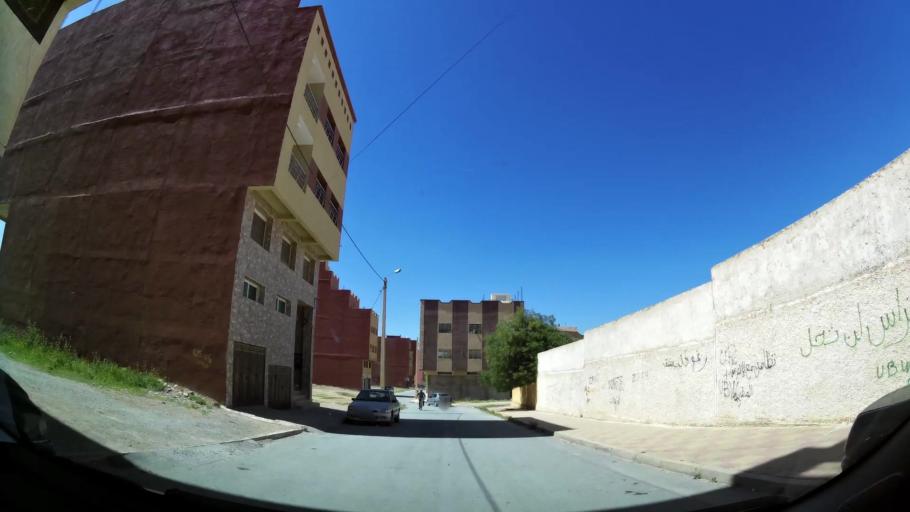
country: MA
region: Oriental
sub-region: Oujda-Angad
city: Oujda
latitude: 34.6650
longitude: -1.8742
